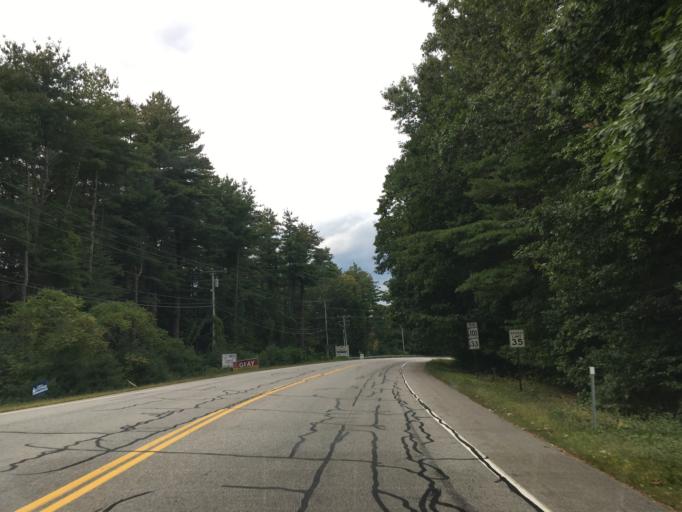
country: US
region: New Hampshire
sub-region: Rockingham County
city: Exeter
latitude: 42.9784
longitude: -70.9187
